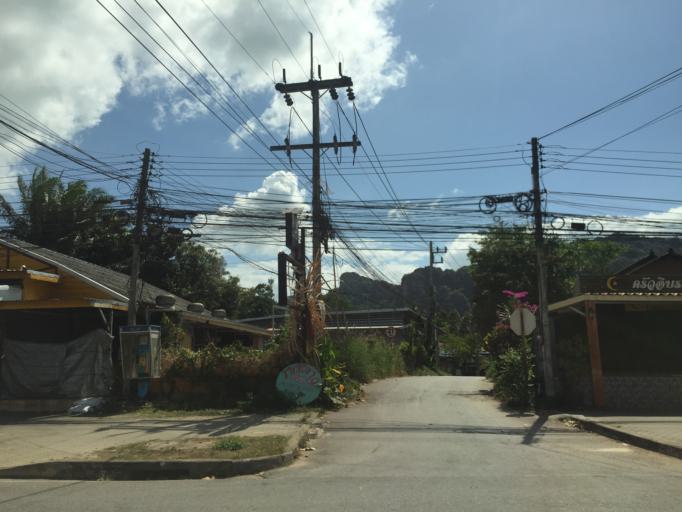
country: TH
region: Phangnga
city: Ban Ao Nang
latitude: 8.0396
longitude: 98.8353
